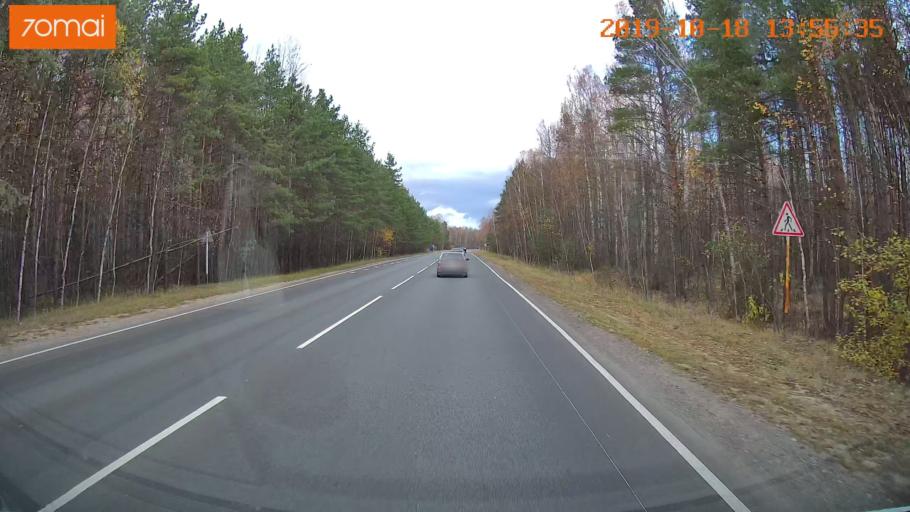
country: RU
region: Rjazan
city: Spas-Klepiki
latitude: 55.0540
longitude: 40.0241
